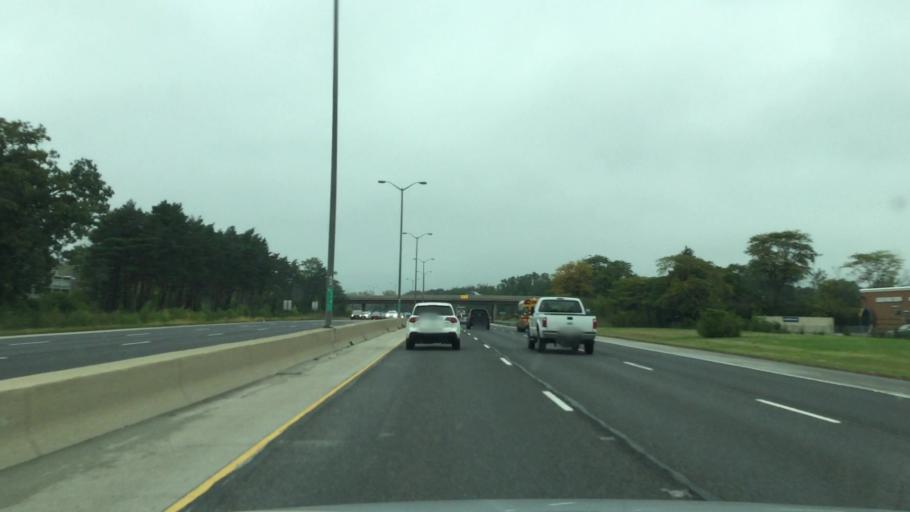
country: US
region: Illinois
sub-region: Cook County
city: Northfield
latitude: 42.0828
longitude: -87.7585
